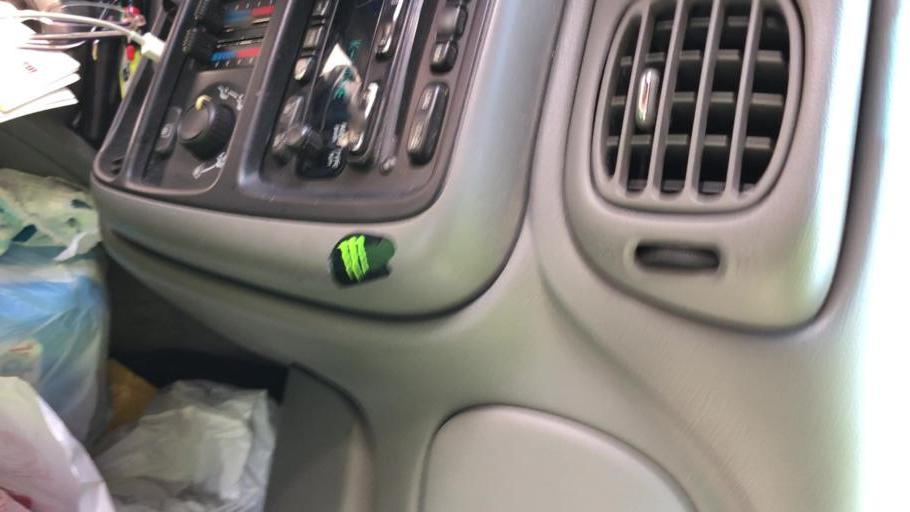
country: US
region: Ohio
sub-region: Champaign County
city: Urbana
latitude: 40.0671
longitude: -83.7357
